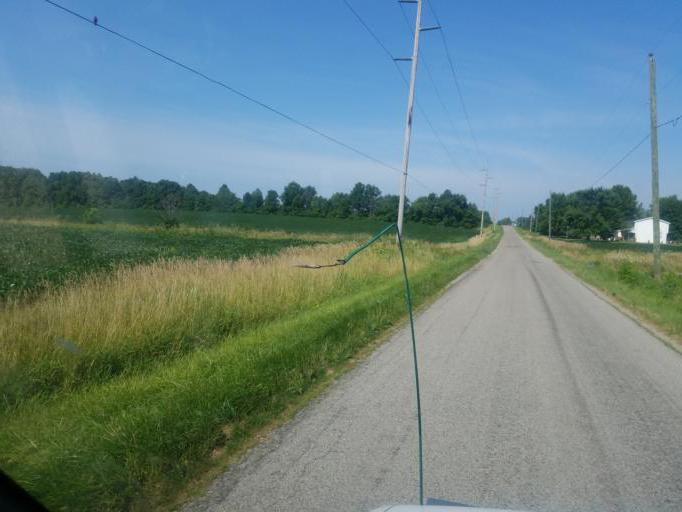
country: US
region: Ohio
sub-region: Union County
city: Marysville
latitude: 40.2885
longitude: -83.3578
